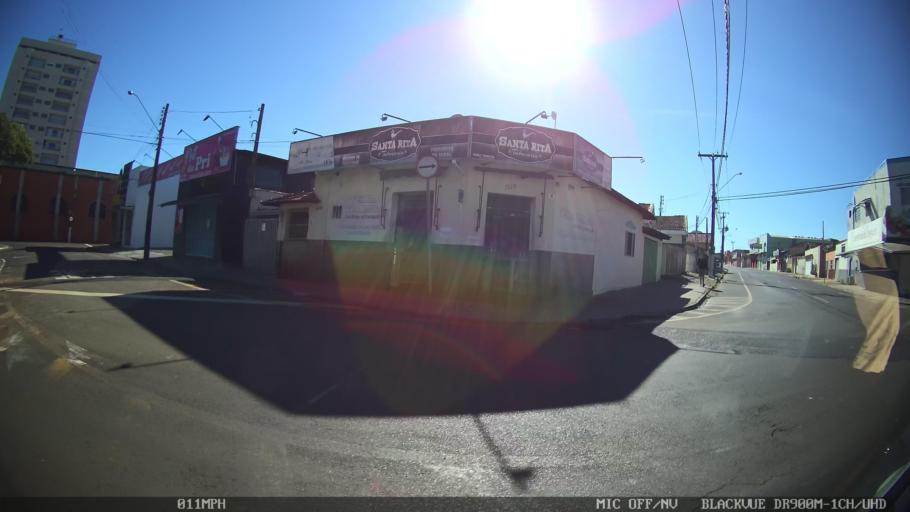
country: BR
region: Sao Paulo
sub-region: Franca
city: Franca
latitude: -20.5481
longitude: -47.3921
